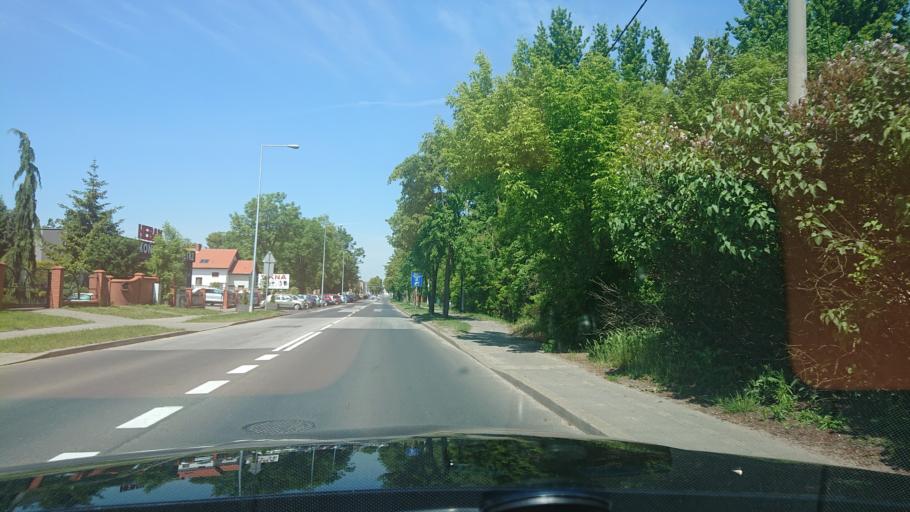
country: PL
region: Greater Poland Voivodeship
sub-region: Powiat gnieznienski
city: Gniezno
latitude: 52.5181
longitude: 17.6085
